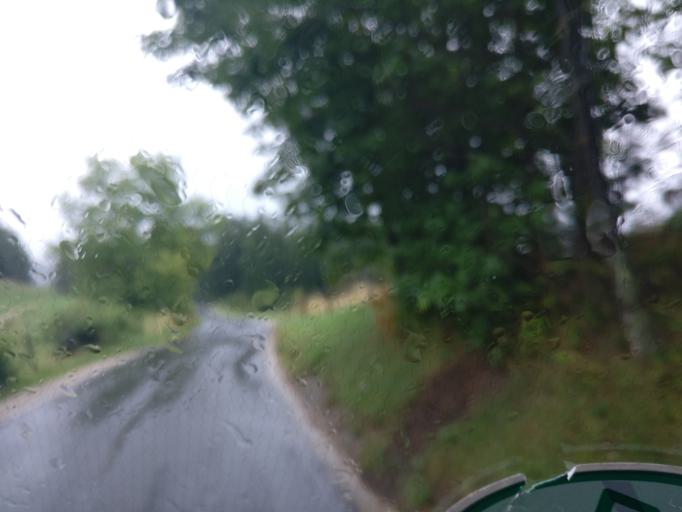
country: AT
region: Lower Austria
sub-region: Politischer Bezirk Neunkirchen
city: Gloggnitz
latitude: 47.6699
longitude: 15.9227
